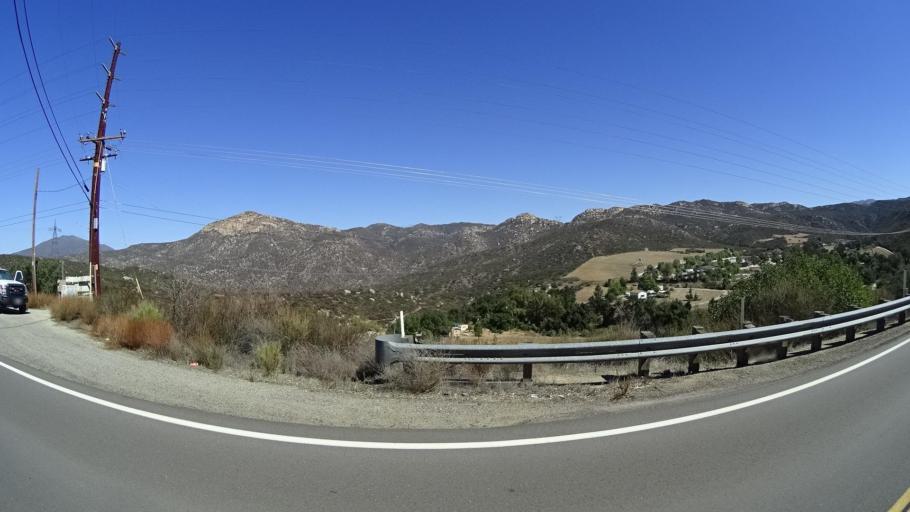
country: US
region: California
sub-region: San Diego County
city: Alpine
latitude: 32.7766
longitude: -116.7121
